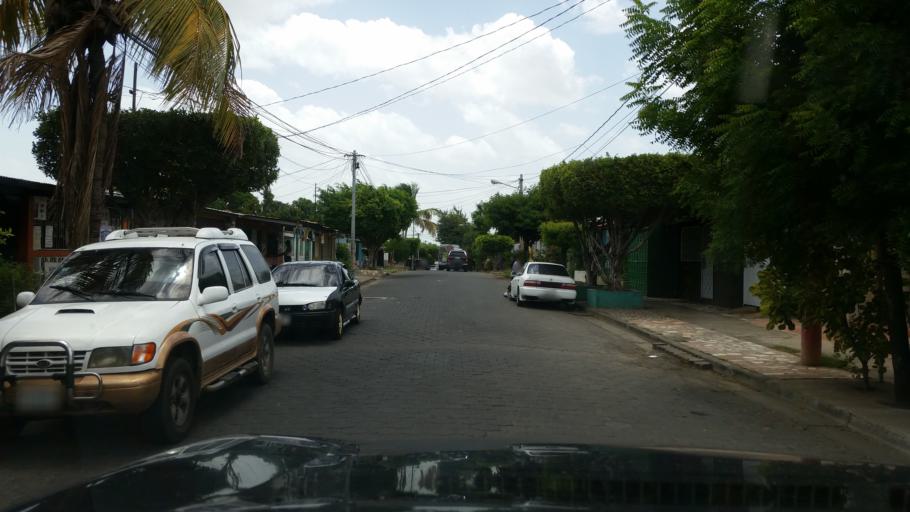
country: NI
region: Managua
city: Managua
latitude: 12.1404
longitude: -86.2101
